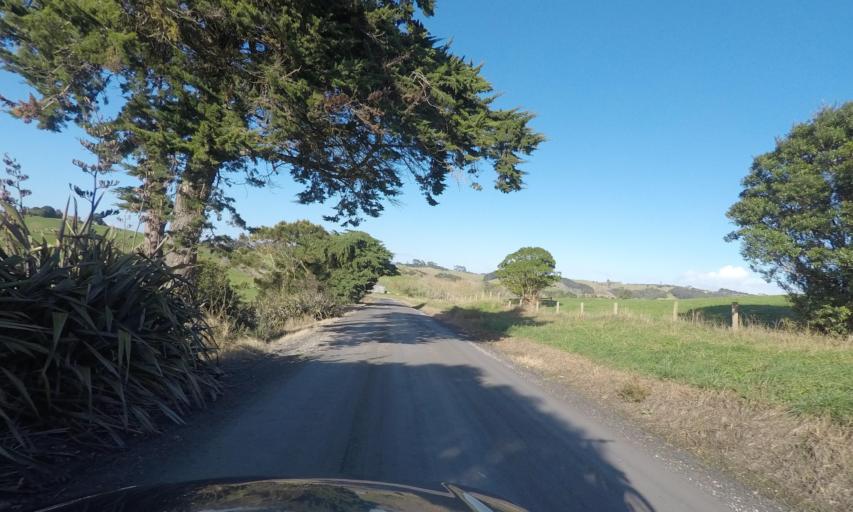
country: NZ
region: Auckland
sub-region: Auckland
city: Wellsford
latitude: -36.1567
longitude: 174.6020
